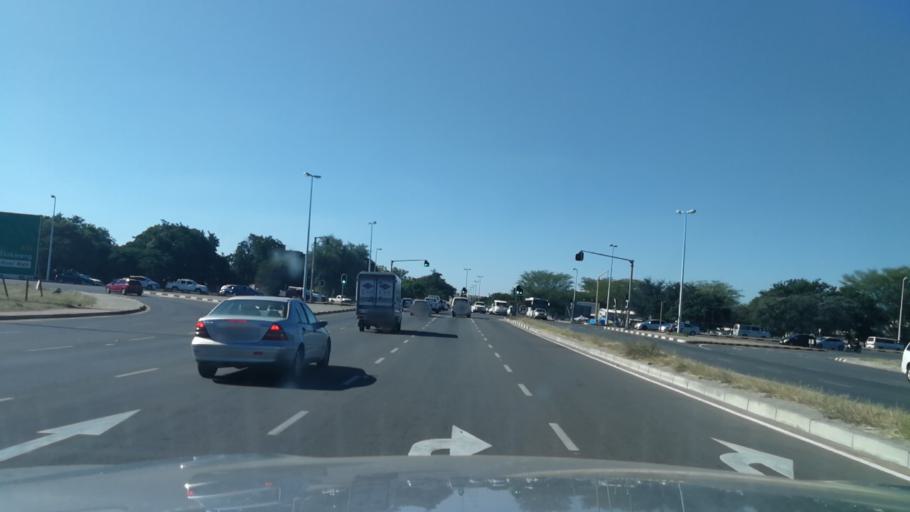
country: BW
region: South East
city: Gaborone
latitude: -24.6732
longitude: 25.9237
